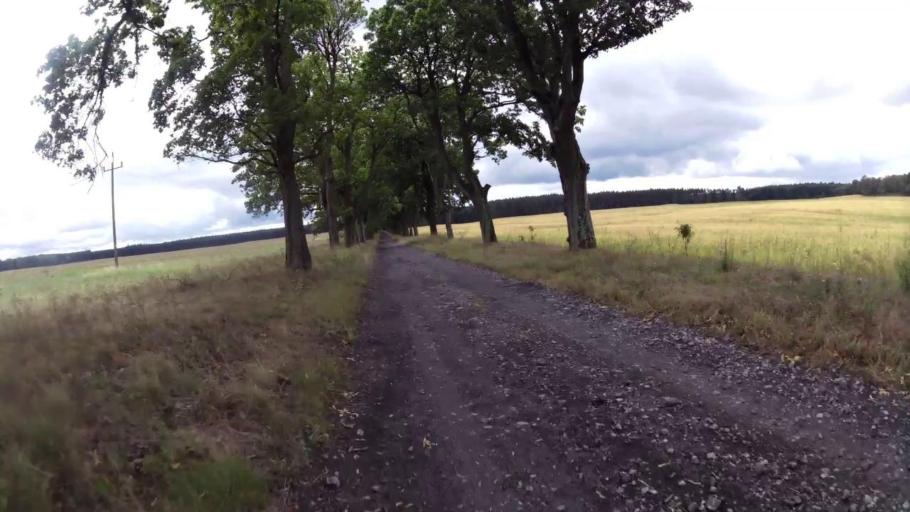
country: PL
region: West Pomeranian Voivodeship
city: Trzcinsko Zdroj
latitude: 52.8769
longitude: 14.7120
